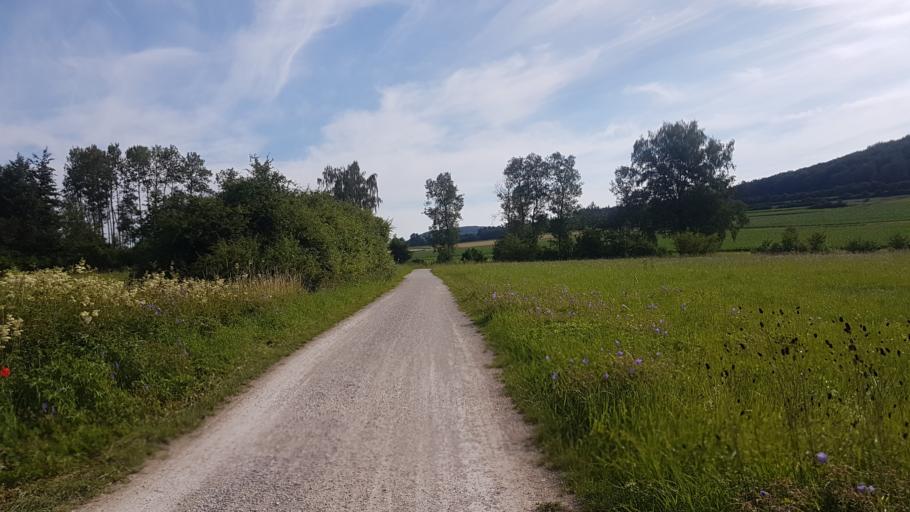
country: DE
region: Bavaria
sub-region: Regierungsbezirk Mittelfranken
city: Treuchtlingen
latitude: 48.9719
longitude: 10.9157
